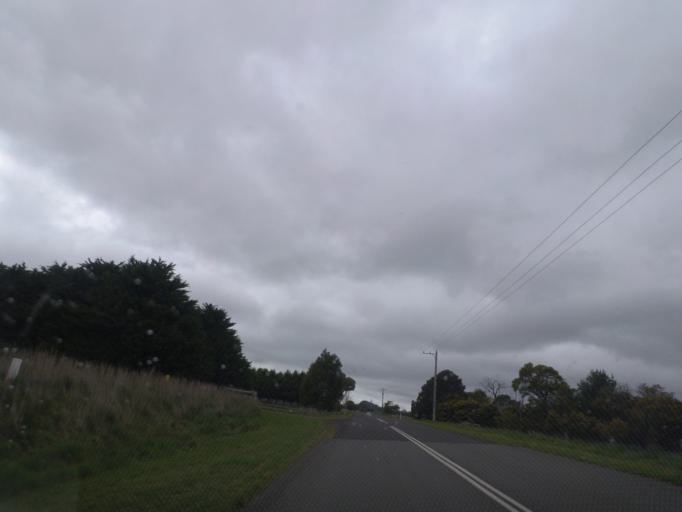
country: AU
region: Victoria
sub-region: Hume
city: Sunbury
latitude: -37.3240
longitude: 144.5478
